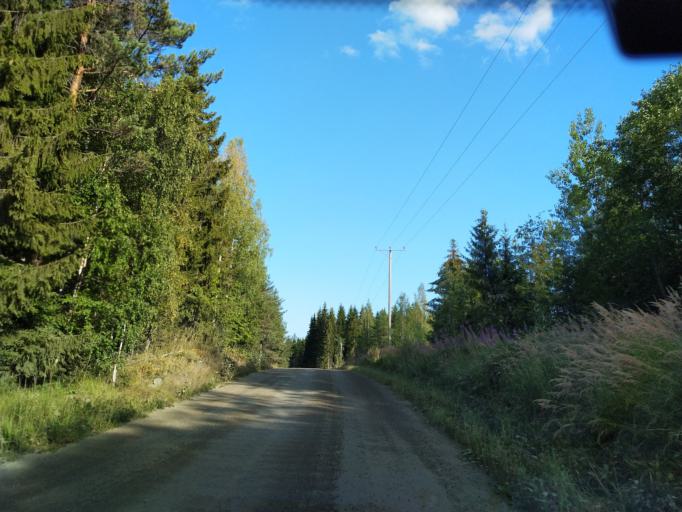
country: FI
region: Central Finland
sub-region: Jaemsae
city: Kuhmoinen
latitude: 61.6913
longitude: 24.9527
